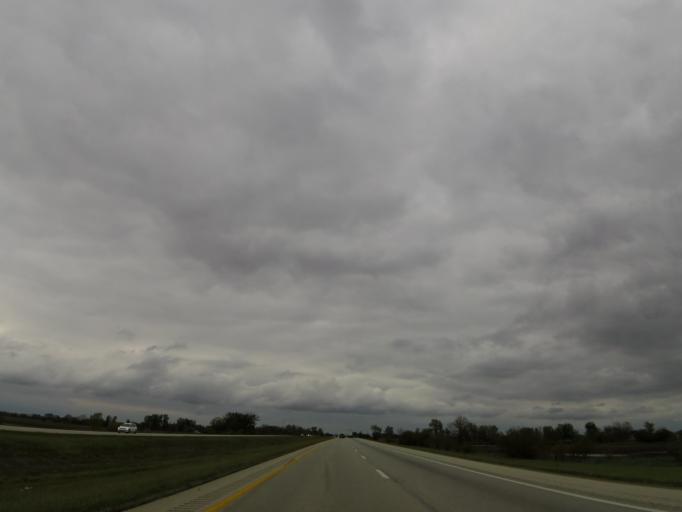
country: US
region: Ohio
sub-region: Greene County
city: Jamestown
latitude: 39.5685
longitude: -83.7011
